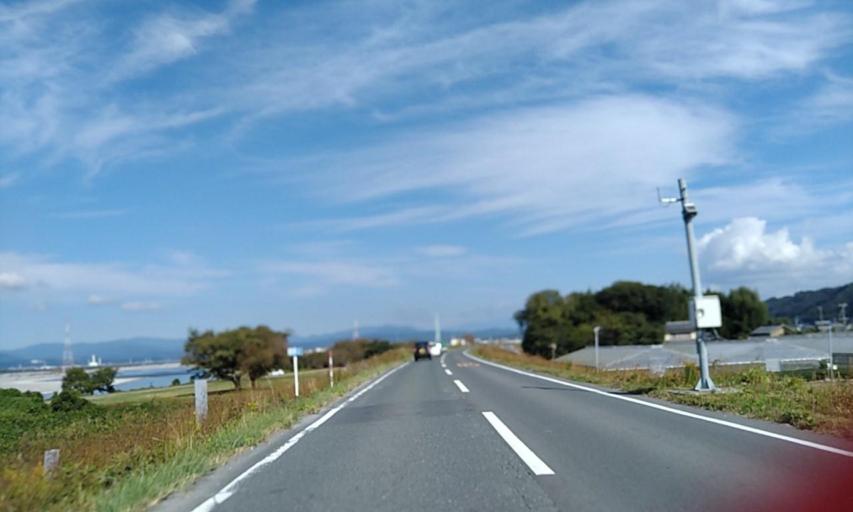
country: JP
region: Shizuoka
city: Hamakita
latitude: 34.7794
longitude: 137.8291
